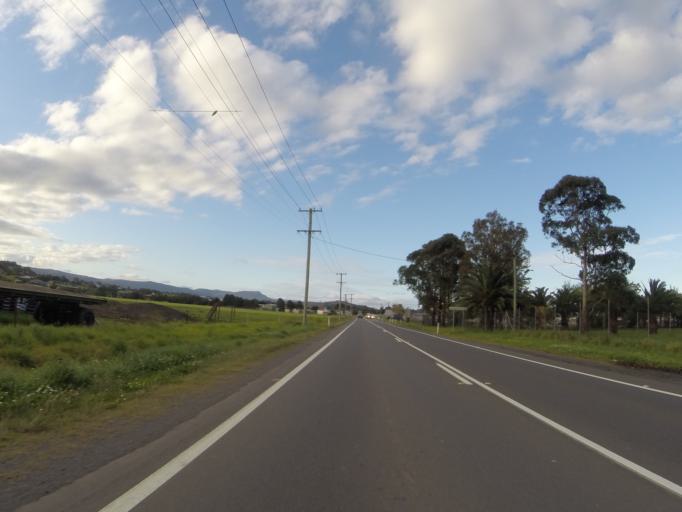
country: AU
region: New South Wales
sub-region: Shellharbour
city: Albion Park Rail
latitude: -34.5520
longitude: 150.7828
